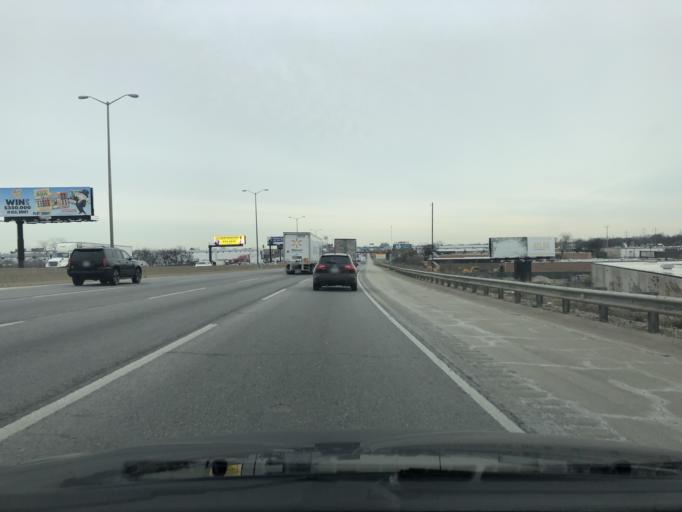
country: US
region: Illinois
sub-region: Cook County
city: Northlake
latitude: 41.9373
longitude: -87.9124
